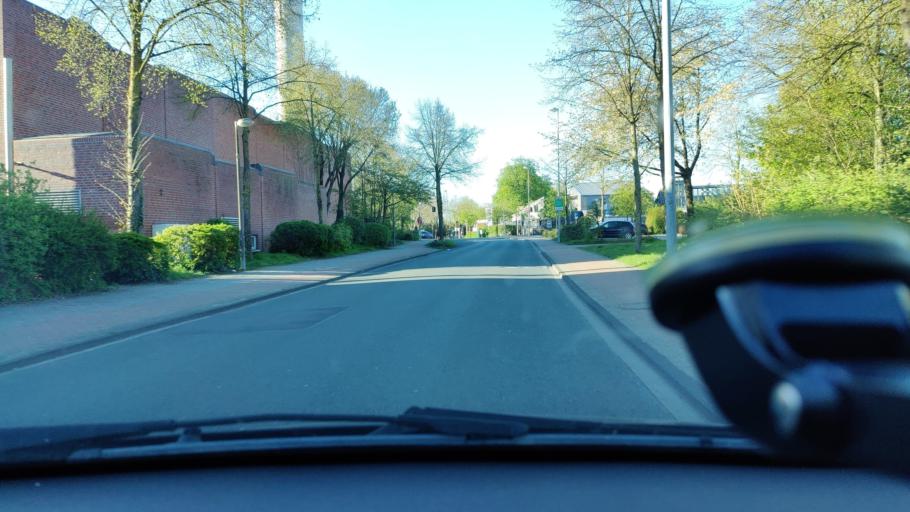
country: DE
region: North Rhine-Westphalia
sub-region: Regierungsbezirk Munster
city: Ahaus
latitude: 52.0810
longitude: 7.0159
